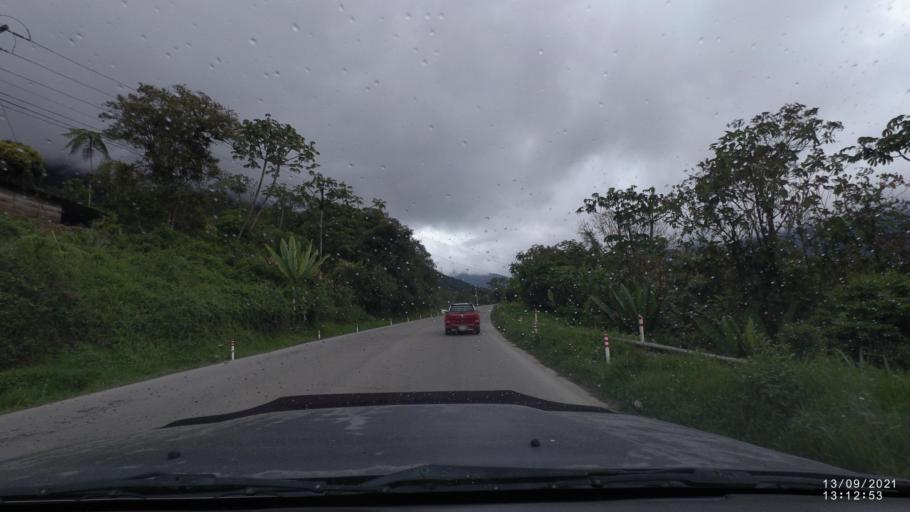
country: BO
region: Cochabamba
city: Colomi
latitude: -17.1990
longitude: -65.8392
